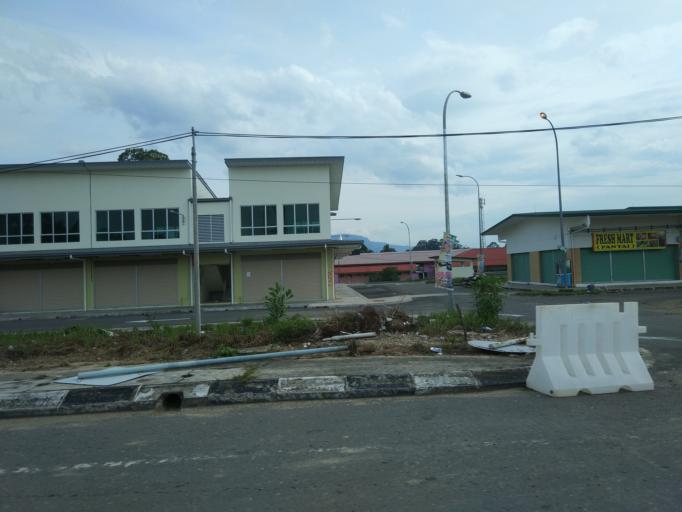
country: MY
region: Sabah
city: Bandar Labuan
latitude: 4.9623
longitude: 115.5072
